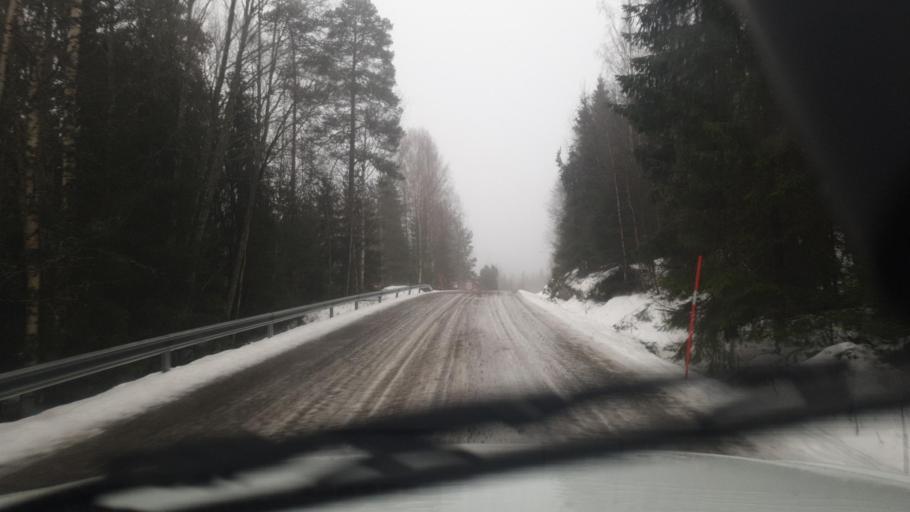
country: SE
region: Vaermland
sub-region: Eda Kommun
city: Charlottenberg
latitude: 60.0226
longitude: 12.6187
